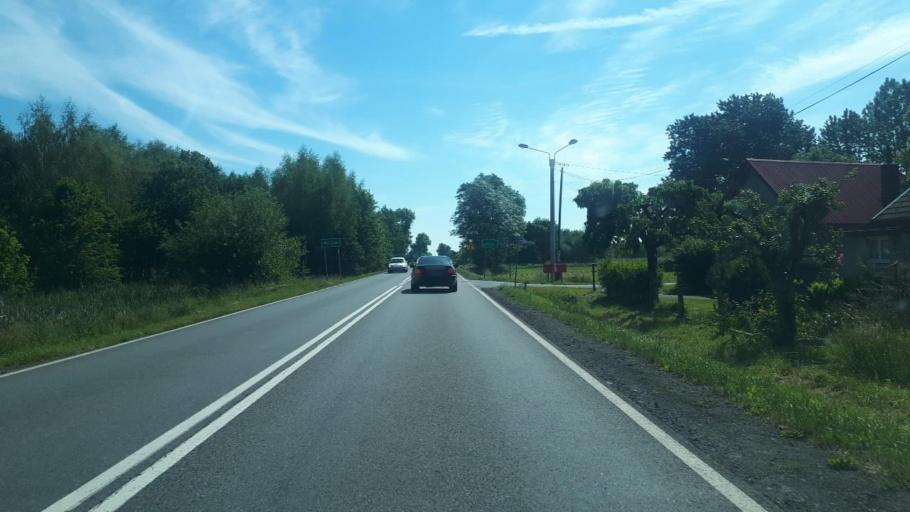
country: PL
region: Silesian Voivodeship
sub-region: Powiat pszczynski
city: Gora
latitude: 49.9706
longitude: 19.0799
